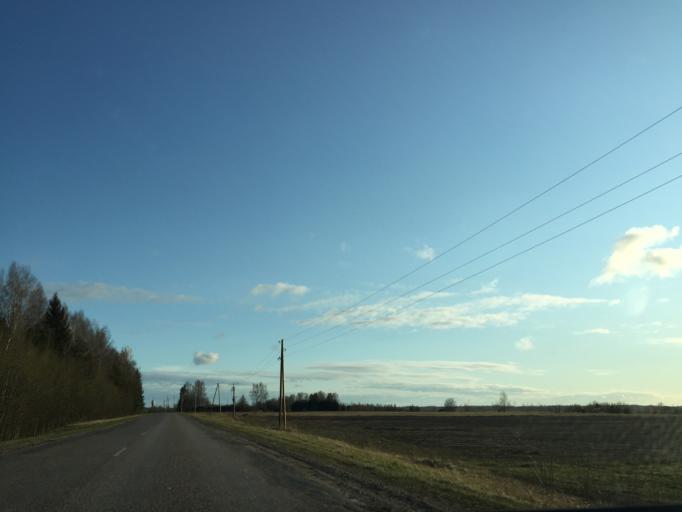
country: LV
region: Limbazu Rajons
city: Limbazi
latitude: 57.5318
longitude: 24.7390
